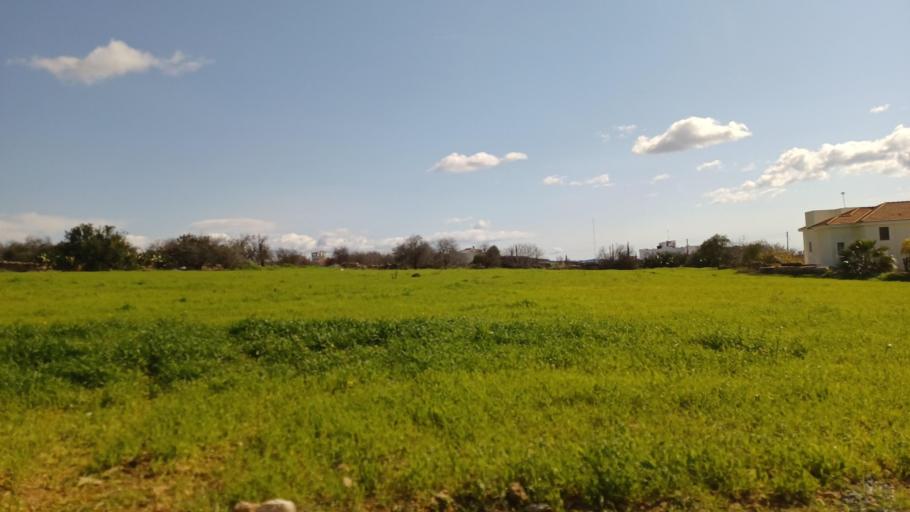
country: CY
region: Pafos
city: Mesogi
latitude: 34.7456
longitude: 32.5348
